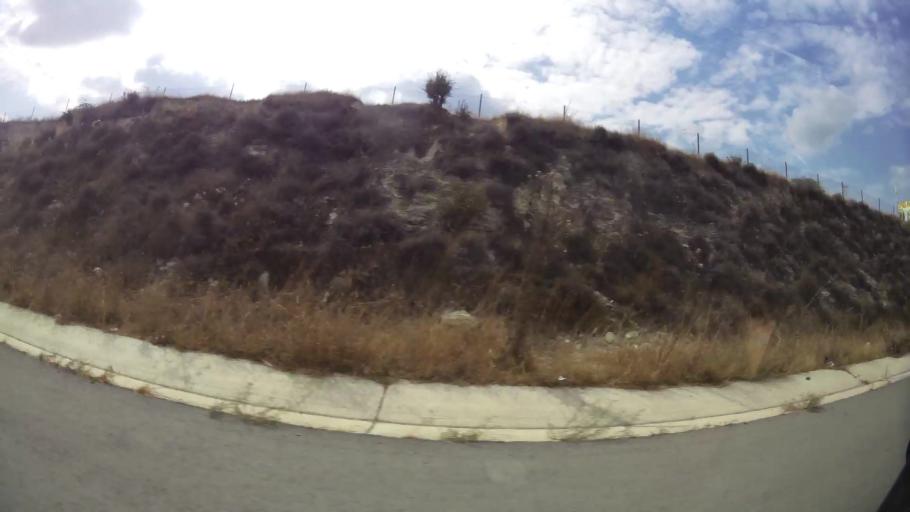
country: CY
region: Lefkosia
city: Lympia
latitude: 34.9933
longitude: 33.4502
